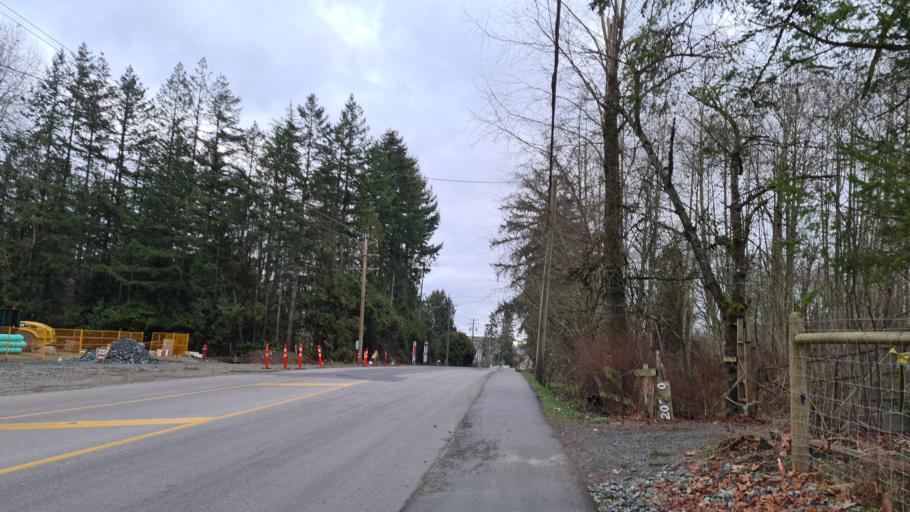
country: CA
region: British Columbia
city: Walnut Grove
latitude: 49.1481
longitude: -122.6597
